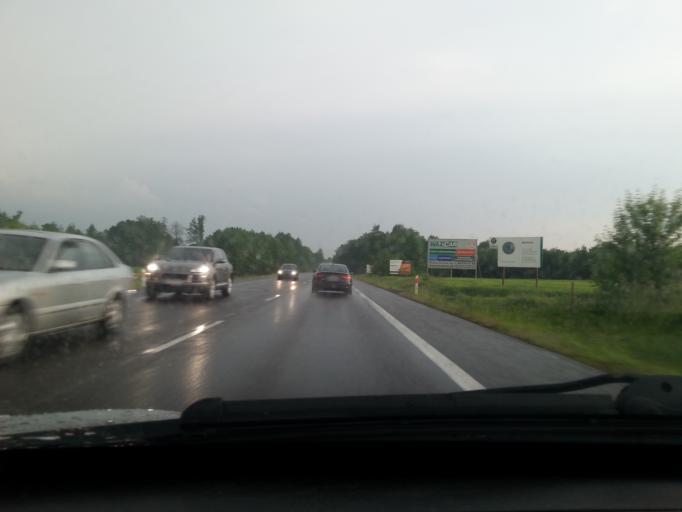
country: PL
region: Lodz Voivodeship
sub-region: Powiat zgierski
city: Strykow
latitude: 51.8722
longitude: 19.5740
